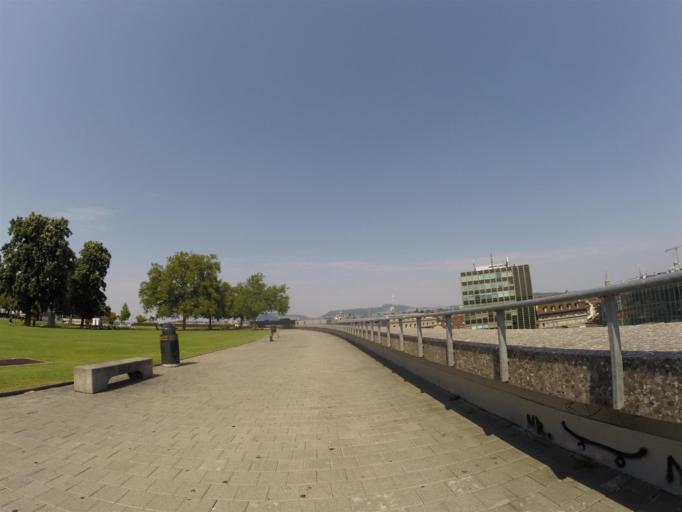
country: CH
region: Bern
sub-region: Bern-Mittelland District
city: Bern
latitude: 46.9495
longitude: 7.4386
